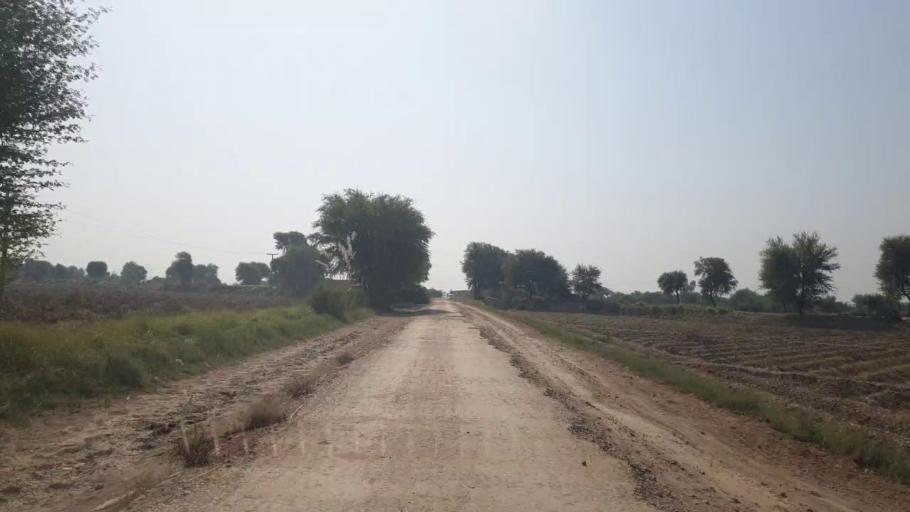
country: PK
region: Sindh
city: Shahdadpur
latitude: 25.9088
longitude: 68.7425
